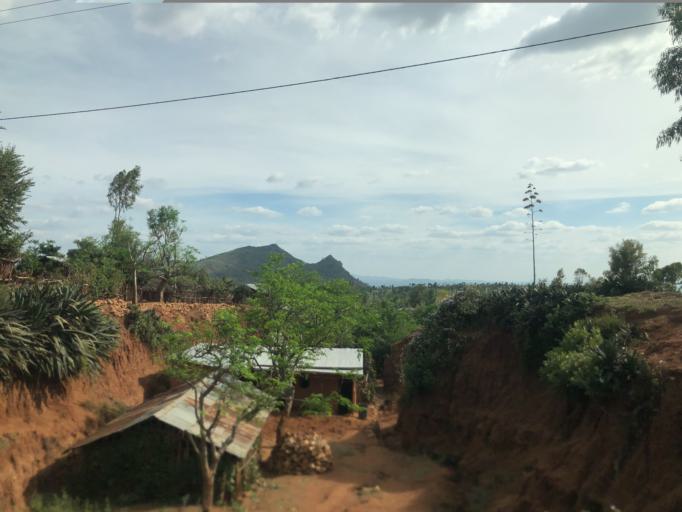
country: ET
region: Southern Nations, Nationalities, and People's Region
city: Konso
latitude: 5.2762
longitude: 37.3458
